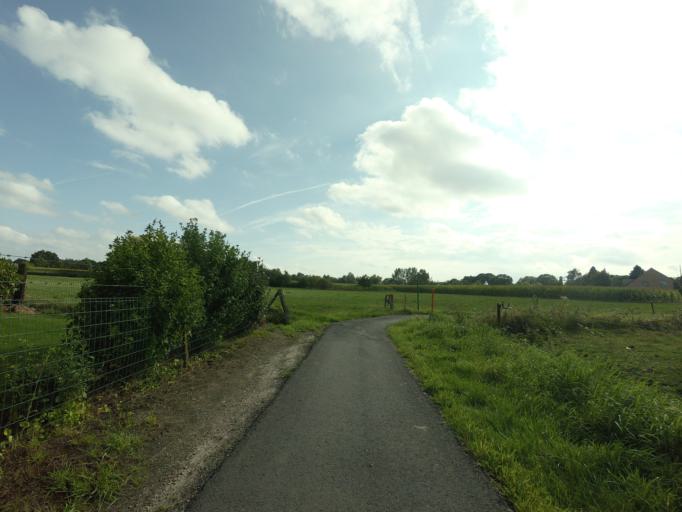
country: BE
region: Flanders
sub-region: Provincie Antwerpen
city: Aartselaar
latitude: 51.1126
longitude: 4.3961
